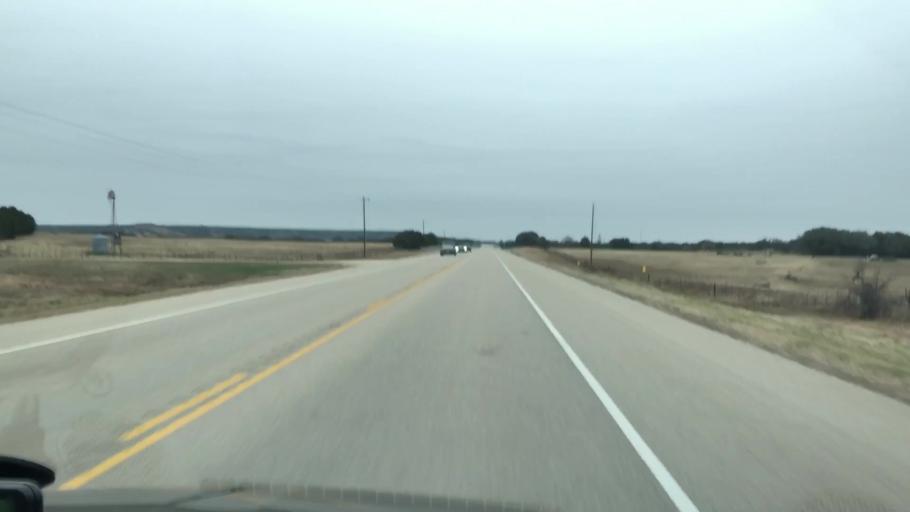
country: US
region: Texas
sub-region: Hamilton County
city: Hamilton
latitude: 31.4991
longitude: -98.1474
